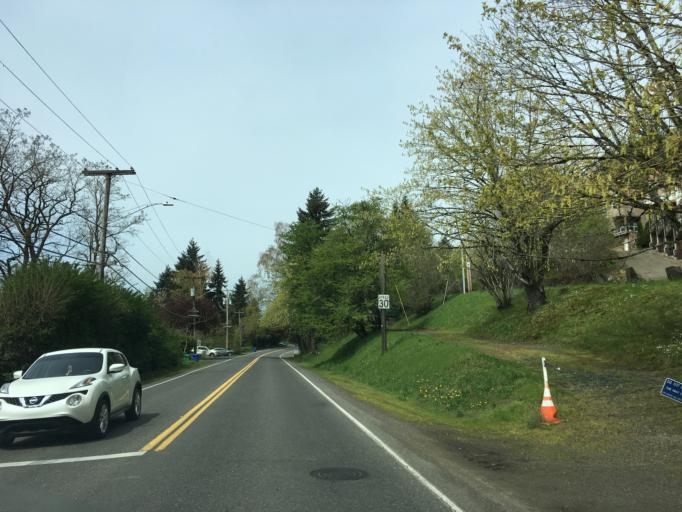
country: US
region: Oregon
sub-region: Multnomah County
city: Lents
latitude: 45.5409
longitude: -122.5687
